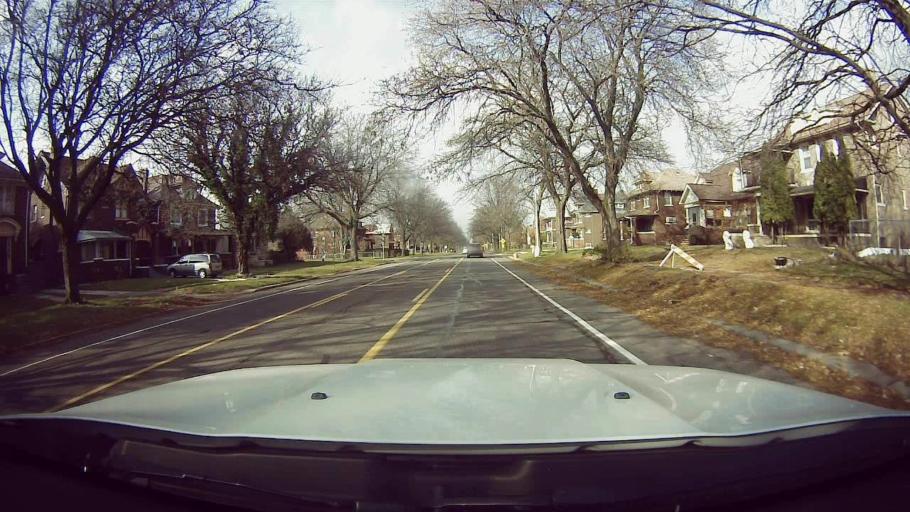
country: US
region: Michigan
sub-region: Wayne County
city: Highland Park
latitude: 42.3621
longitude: -83.1121
